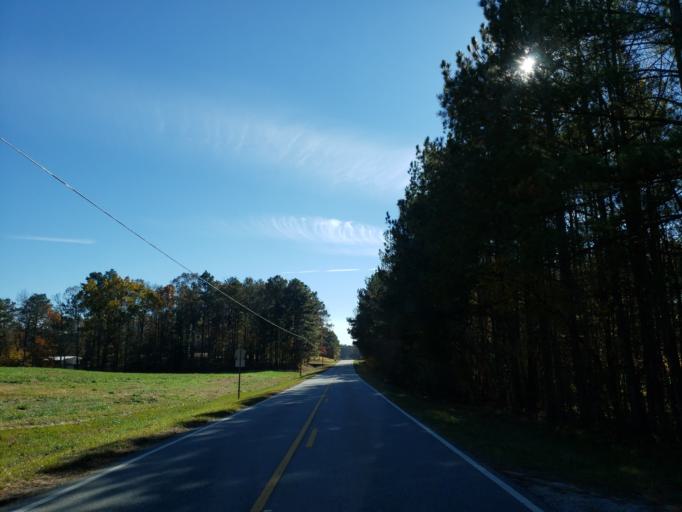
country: US
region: Alabama
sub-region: Cleburne County
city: Heflin
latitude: 33.5854
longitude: -85.6380
